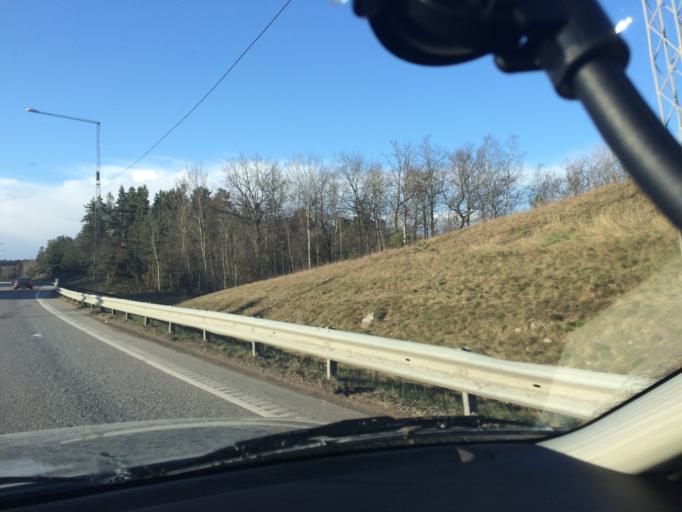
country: SE
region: Stockholm
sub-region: Jarfalla Kommun
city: Jakobsberg
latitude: 59.4247
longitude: 17.8513
